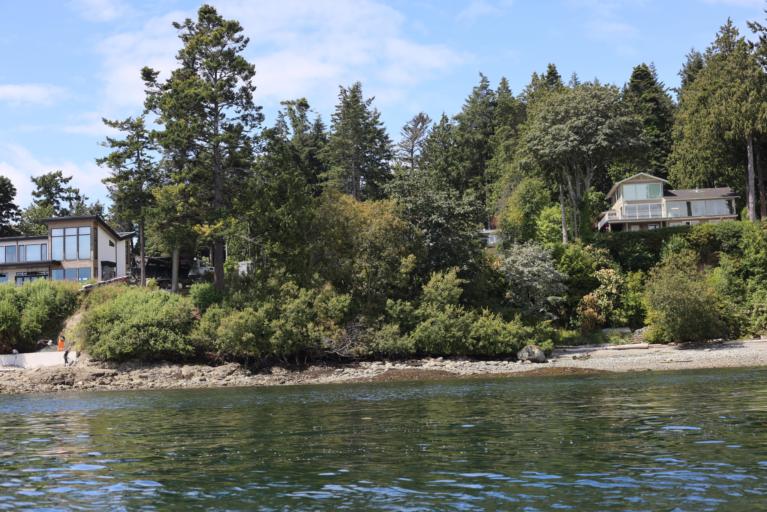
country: CA
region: British Columbia
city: North Saanich
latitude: 48.6063
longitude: -123.3932
